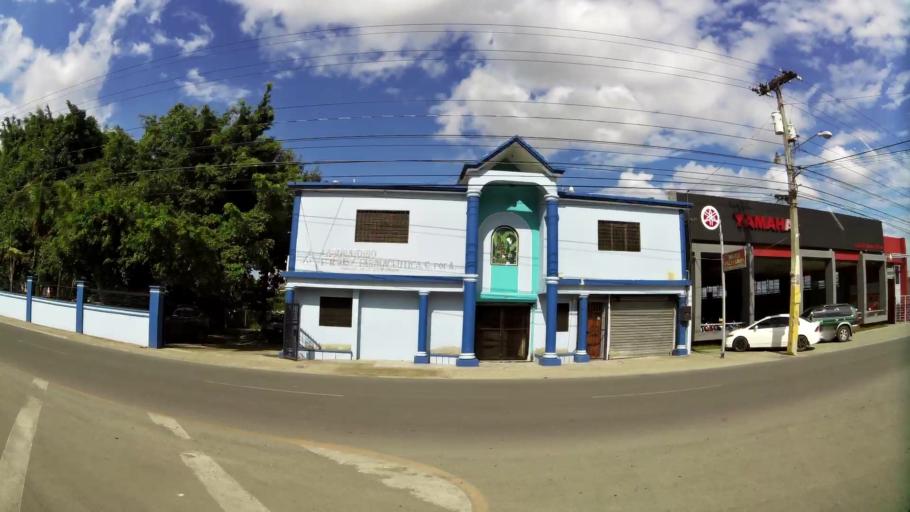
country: DO
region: La Vega
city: Concepcion de La Vega
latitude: 19.2305
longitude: -70.5283
